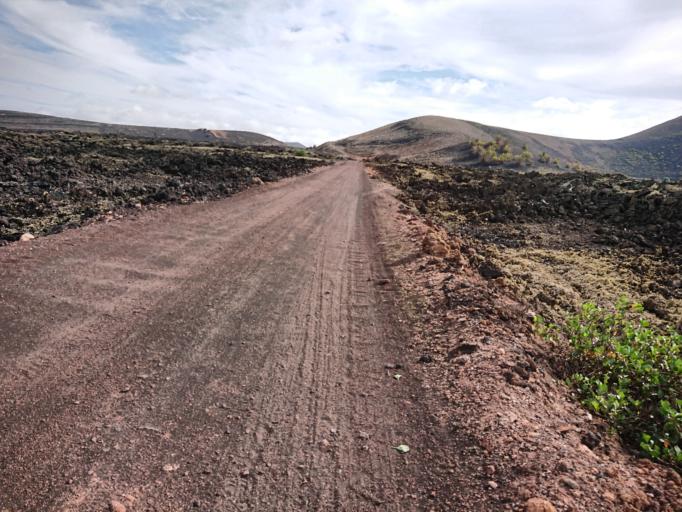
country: ES
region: Canary Islands
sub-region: Provincia de Las Palmas
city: Tinajo
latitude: 29.0222
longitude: -13.6798
